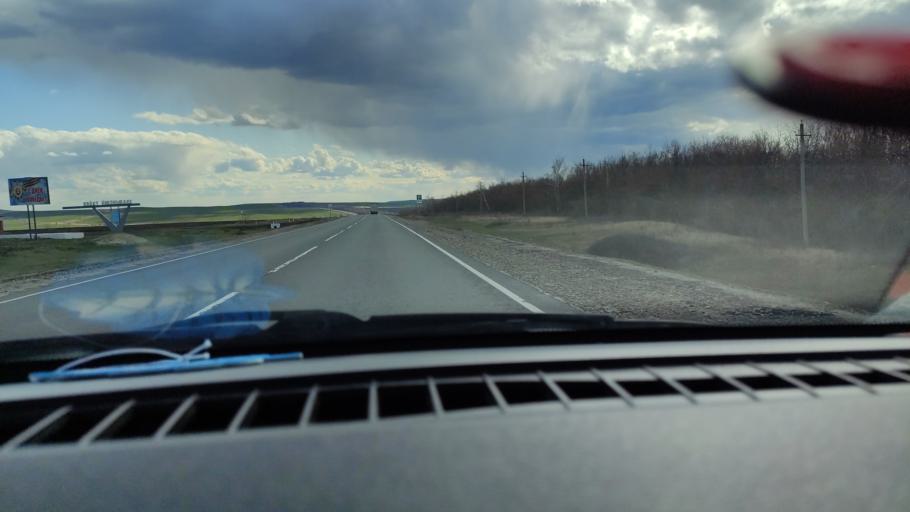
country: RU
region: Saratov
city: Alekseyevka
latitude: 52.2615
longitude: 47.9213
